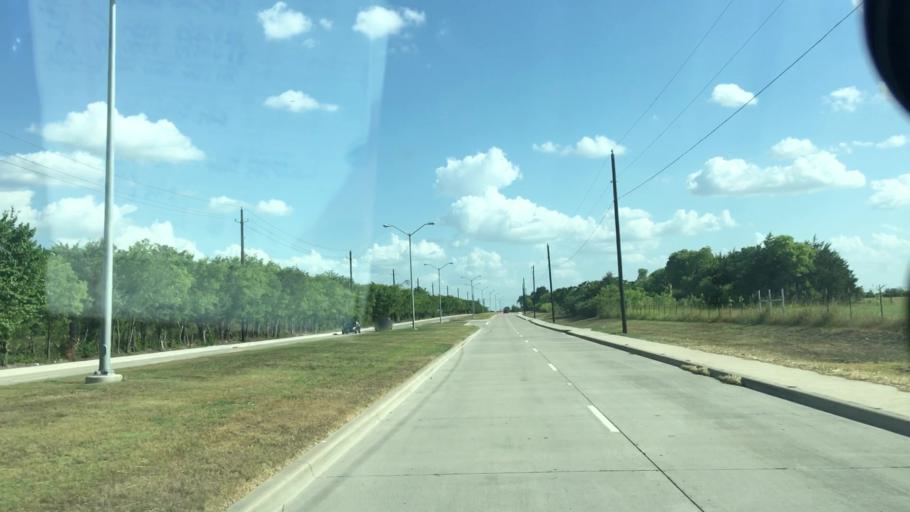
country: US
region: Texas
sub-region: Dallas County
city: Lancaster
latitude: 32.6243
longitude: -96.7530
